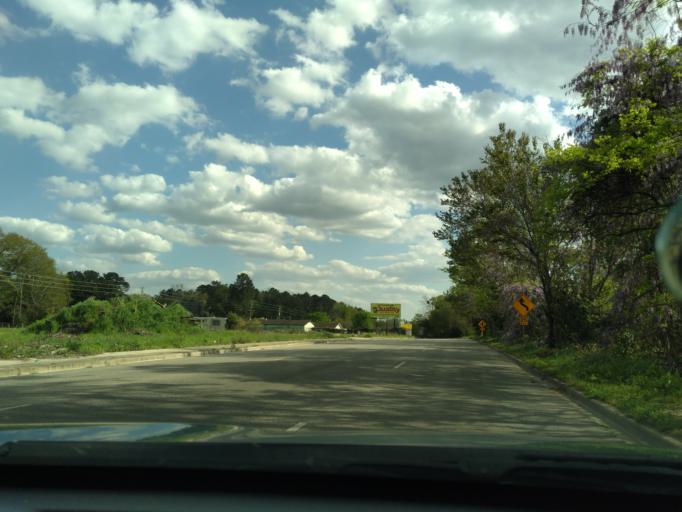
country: US
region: South Carolina
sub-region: Florence County
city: Florence
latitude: 34.1838
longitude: -79.7622
